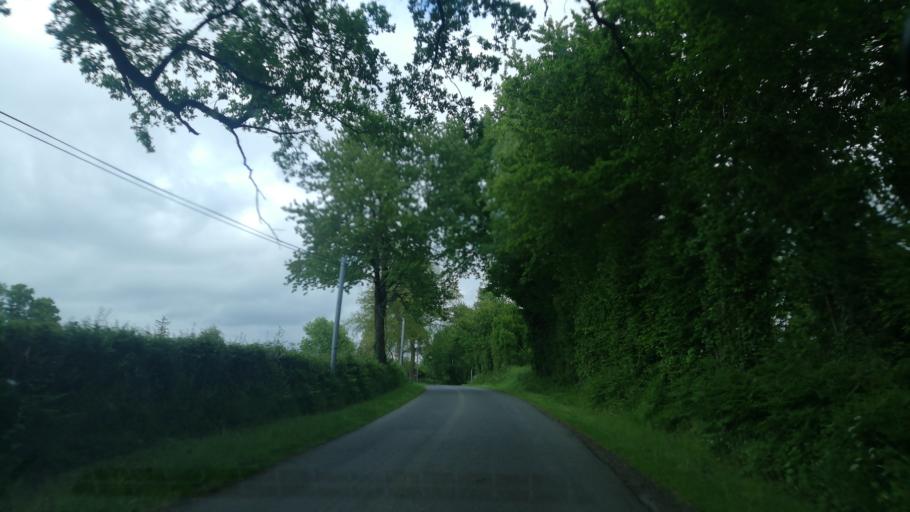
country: FR
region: Poitou-Charentes
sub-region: Departement des Deux-Sevres
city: Moncoutant
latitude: 46.6796
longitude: -0.5789
